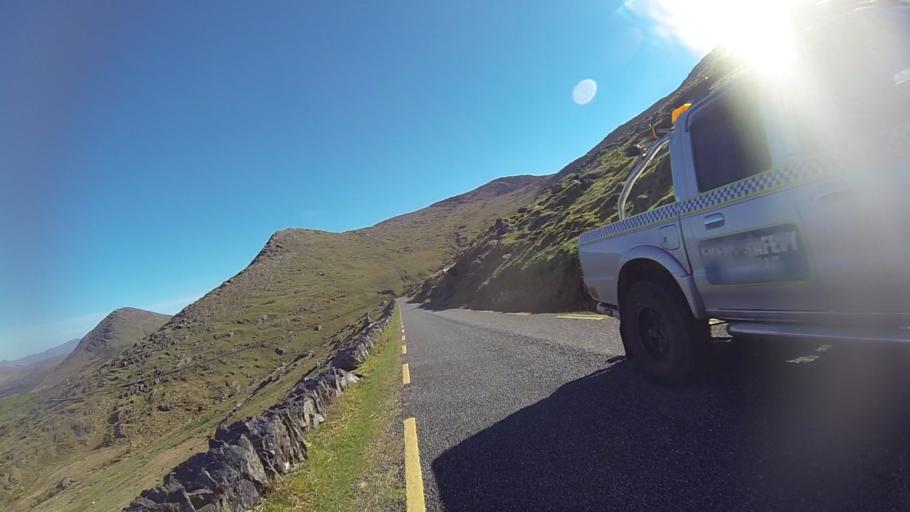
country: IE
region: Munster
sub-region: Ciarrai
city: Kenmare
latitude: 51.7271
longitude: -9.7570
